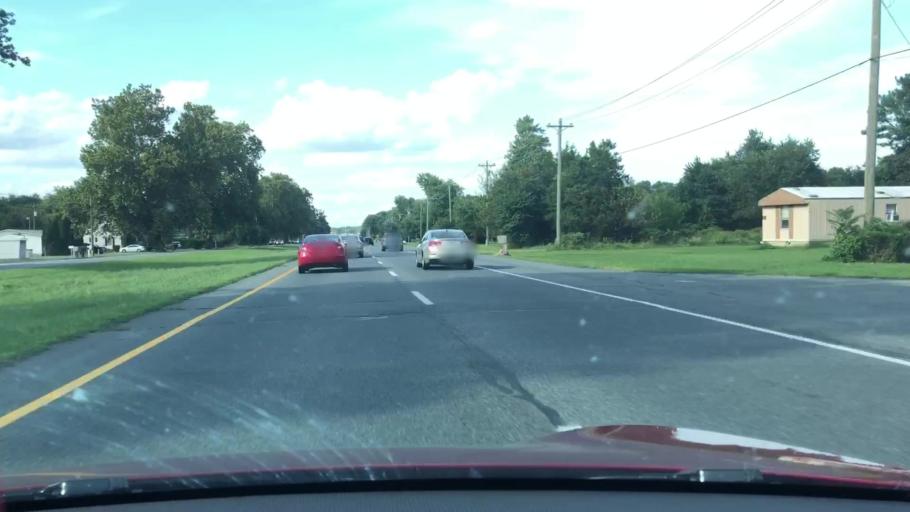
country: US
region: Delaware
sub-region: Kent County
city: Felton
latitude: 39.0304
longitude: -75.5619
